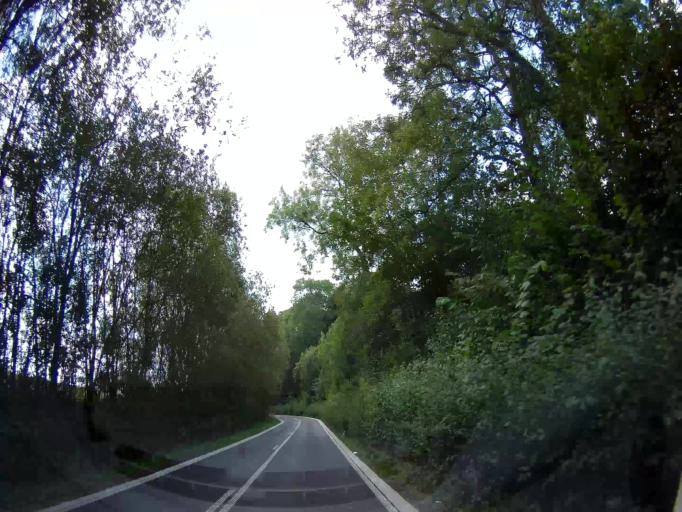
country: BE
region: Wallonia
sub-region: Province de Namur
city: Gesves
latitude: 50.3848
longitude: 5.0749
